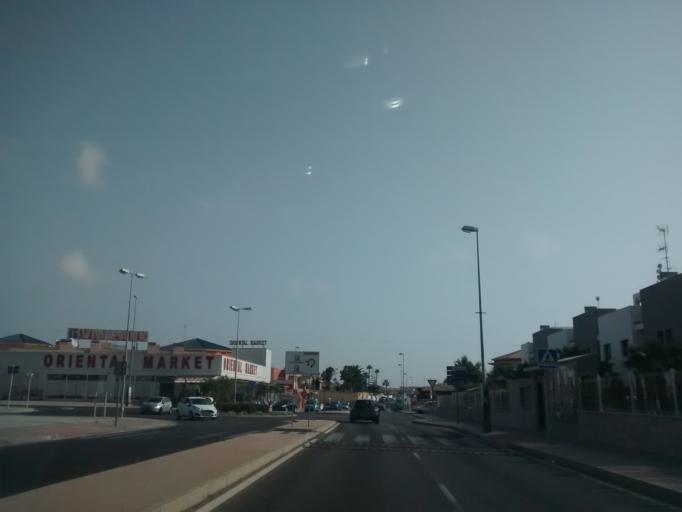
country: ES
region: Valencia
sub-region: Provincia de Alicante
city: Torrevieja
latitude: 37.9306
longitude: -0.7333
